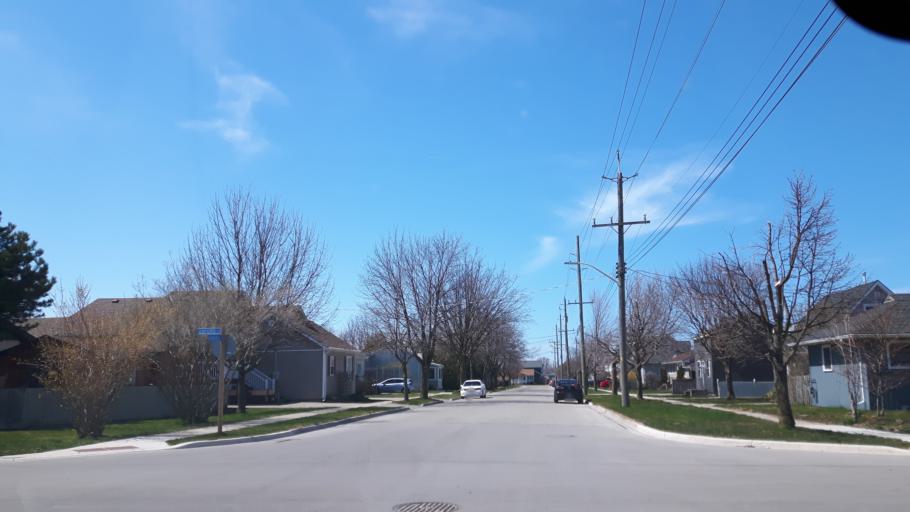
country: CA
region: Ontario
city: Goderich
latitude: 43.7384
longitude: -81.6998
